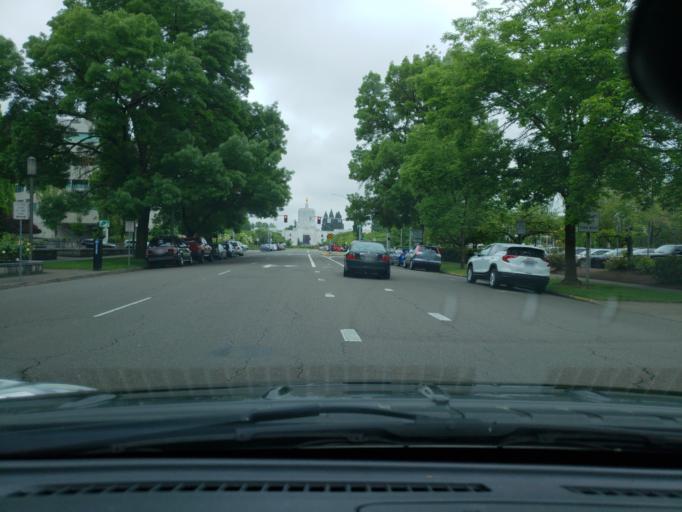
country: US
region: Oregon
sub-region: Marion County
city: Salem
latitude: 44.9431
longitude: -123.0281
